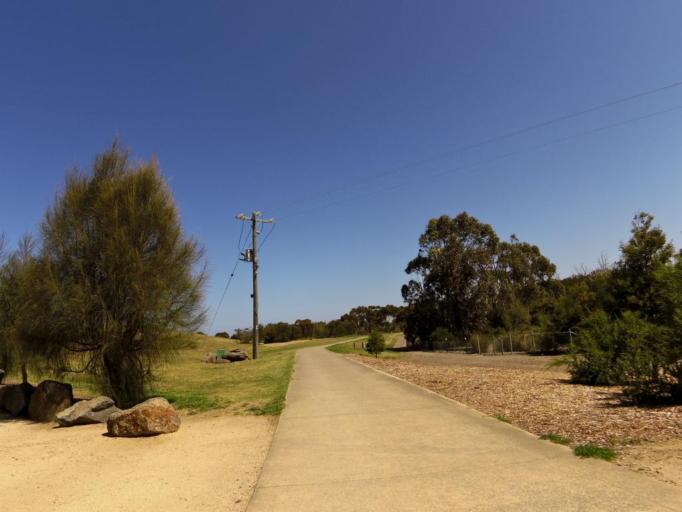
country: AU
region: Victoria
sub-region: Hobsons Bay
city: Altona Meadows
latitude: -37.8821
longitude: 144.7964
